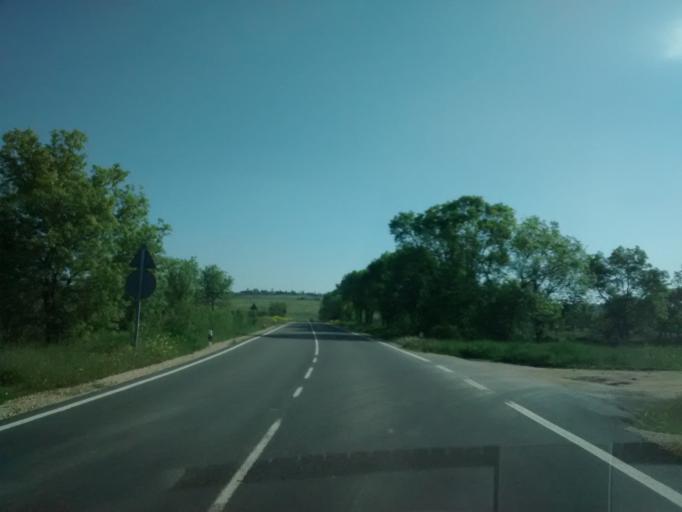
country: ES
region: Castille and Leon
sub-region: Provincia de Segovia
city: Trescasas
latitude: 40.9754
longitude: -4.0266
